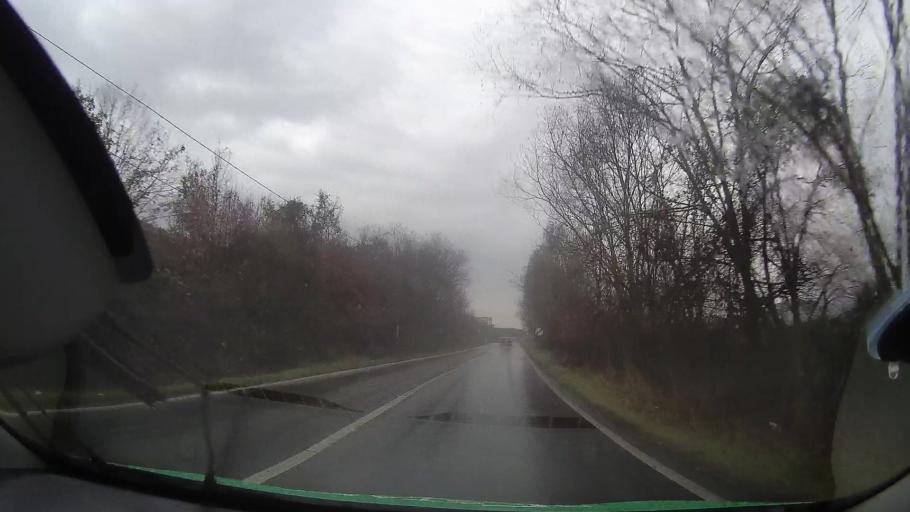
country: RO
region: Bihor
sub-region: Comuna Rabagani
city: Rabagani
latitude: 46.7523
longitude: 22.2101
